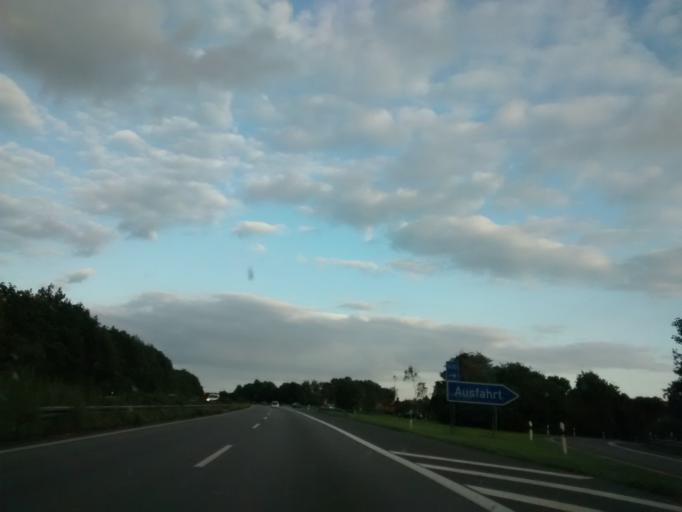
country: DE
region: North Rhine-Westphalia
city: Ibbenburen
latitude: 52.2579
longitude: 7.7075
